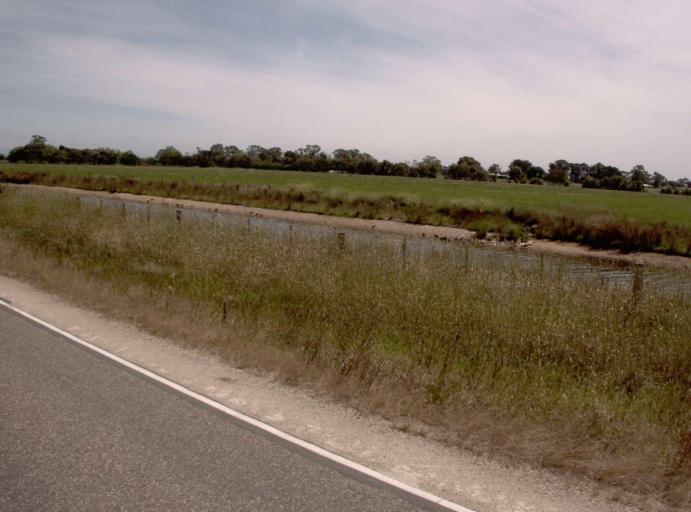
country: AU
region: Victoria
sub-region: Wellington
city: Heyfield
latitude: -38.0493
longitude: 146.8753
